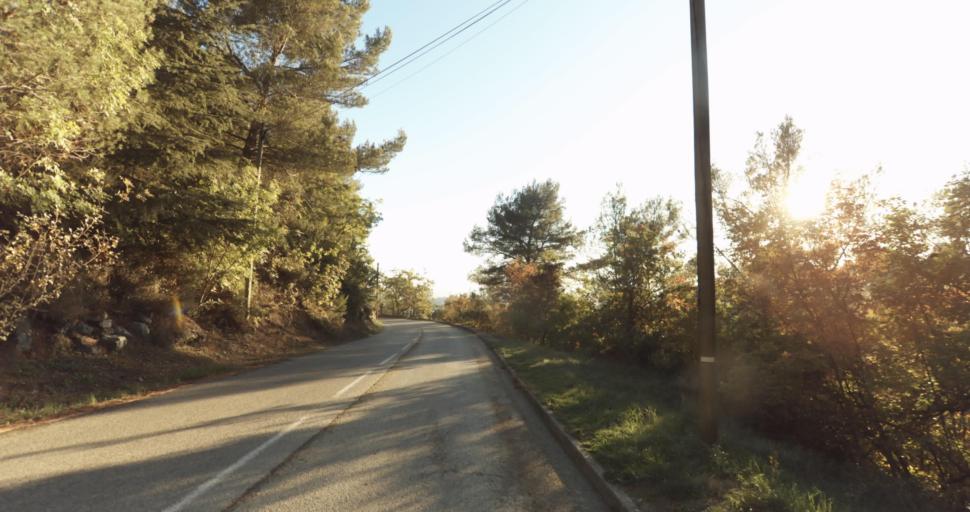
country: FR
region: Provence-Alpes-Cote d'Azur
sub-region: Departement des Alpes-Maritimes
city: Vence
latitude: 43.7355
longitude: 7.1051
